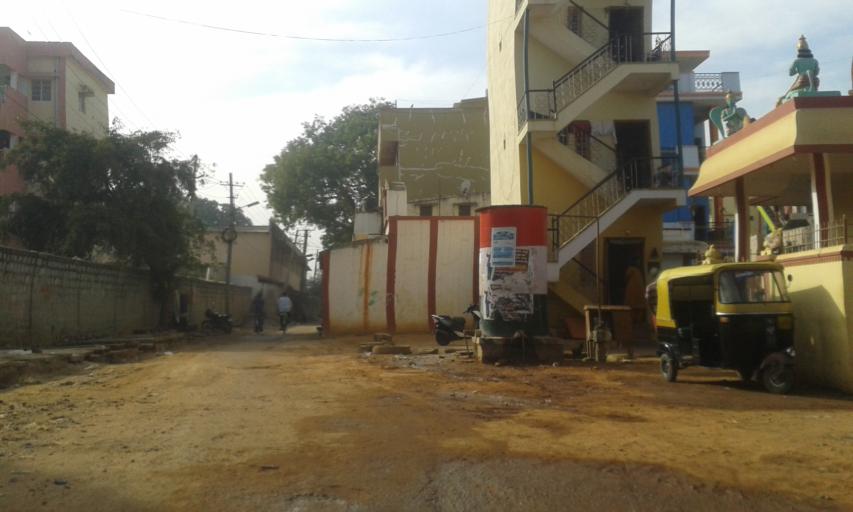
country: IN
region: Karnataka
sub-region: Bangalore Urban
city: Bangalore
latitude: 12.9602
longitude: 77.6184
